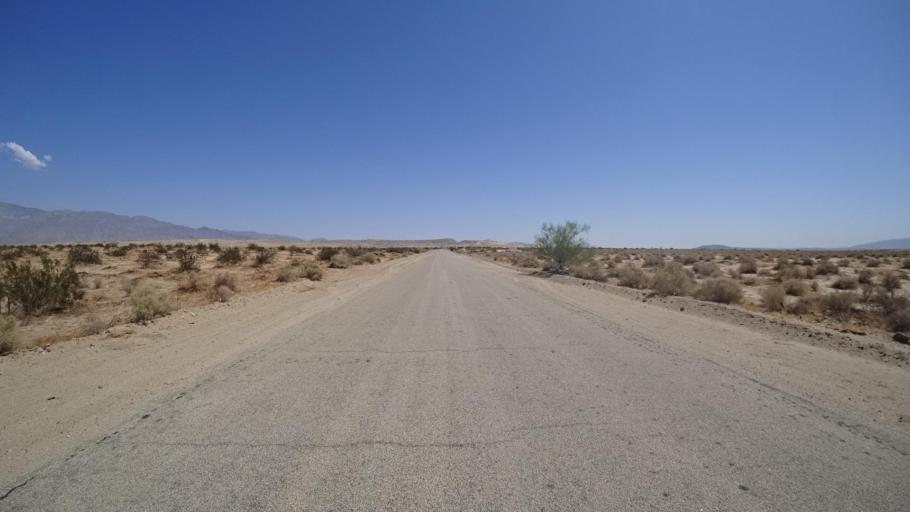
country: US
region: California
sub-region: San Diego County
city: Borrego Springs
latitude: 33.2577
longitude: -116.2989
